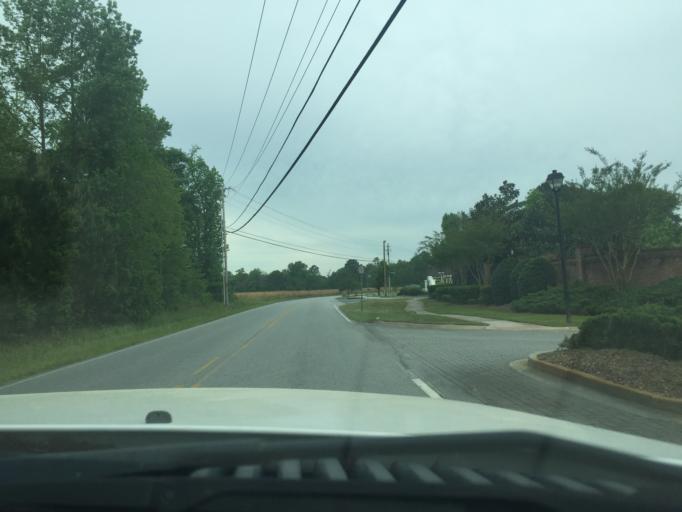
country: US
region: Georgia
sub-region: Chatham County
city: Georgetown
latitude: 31.9697
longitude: -81.2324
